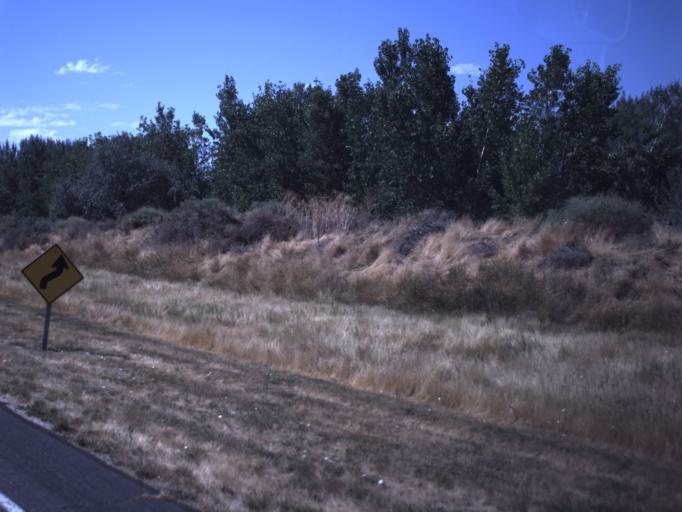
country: US
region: Utah
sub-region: Box Elder County
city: Willard
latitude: 41.4135
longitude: -112.0514
